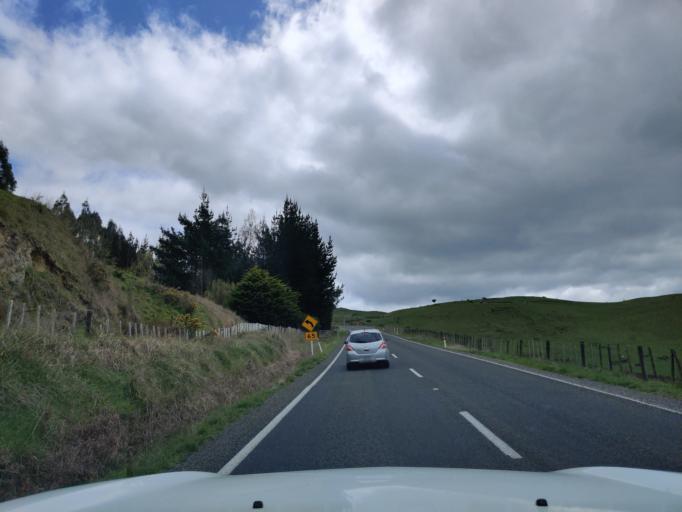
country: NZ
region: Manawatu-Wanganui
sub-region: Wanganui District
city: Wanganui
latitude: -39.7872
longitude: 175.2408
